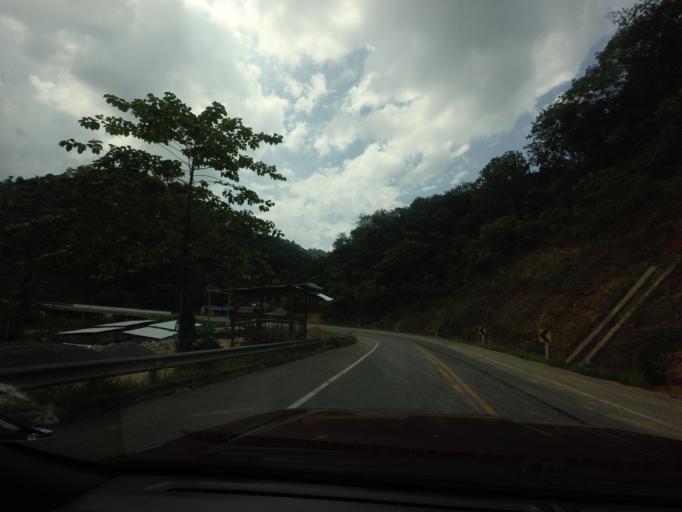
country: TH
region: Yala
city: Than To
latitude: 6.0505
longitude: 101.1973
